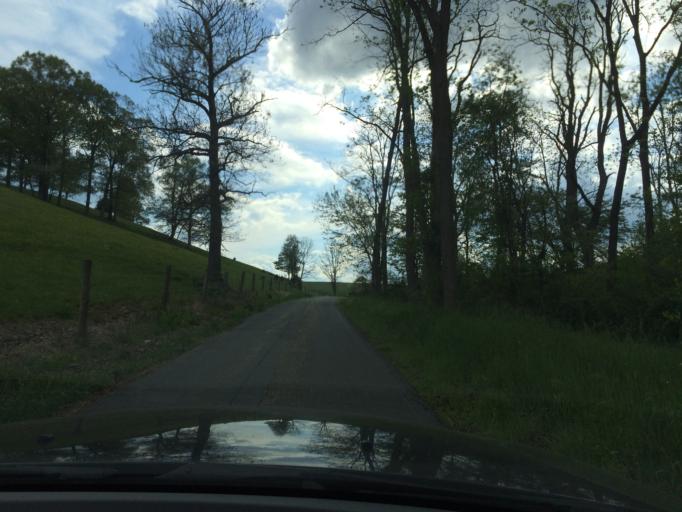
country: US
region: Maryland
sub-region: Carroll County
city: Eldersburg
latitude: 39.4772
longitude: -77.0053
